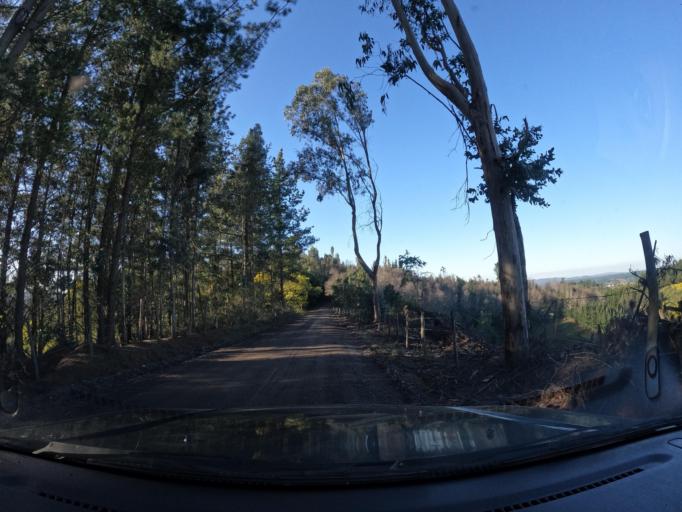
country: CL
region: Biobio
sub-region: Provincia de Concepcion
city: Chiguayante
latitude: -37.0134
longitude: -72.8612
